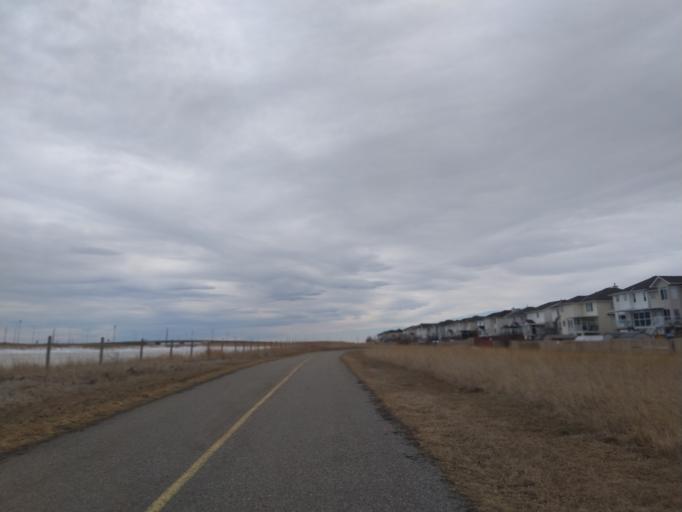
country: CA
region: Alberta
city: Chestermere
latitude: 51.1059
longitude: -113.9224
